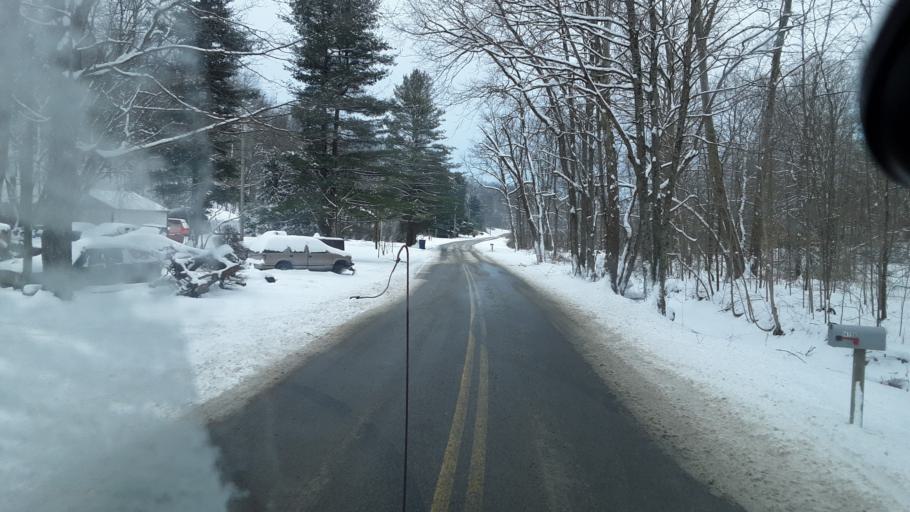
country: US
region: Ohio
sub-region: Perry County
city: Somerset
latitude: 39.9059
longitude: -82.2283
